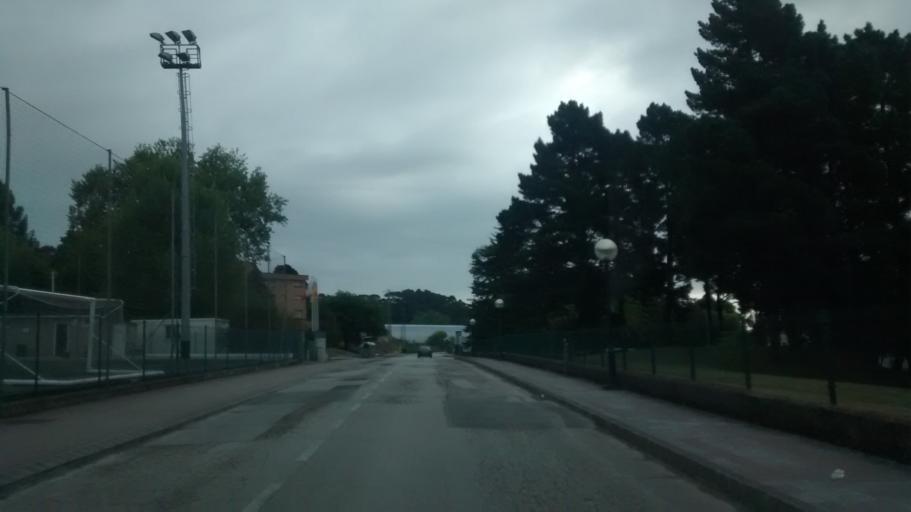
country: ES
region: Cantabria
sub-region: Provincia de Cantabria
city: El Astillero
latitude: 43.4151
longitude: -3.8232
